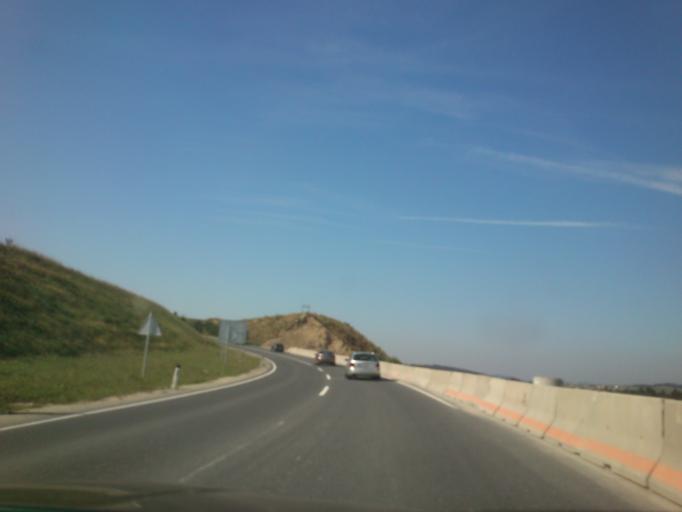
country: AT
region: Upper Austria
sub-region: Politischer Bezirk Urfahr-Umgebung
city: Alberndorf in der Riedmark
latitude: 48.4177
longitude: 14.4895
